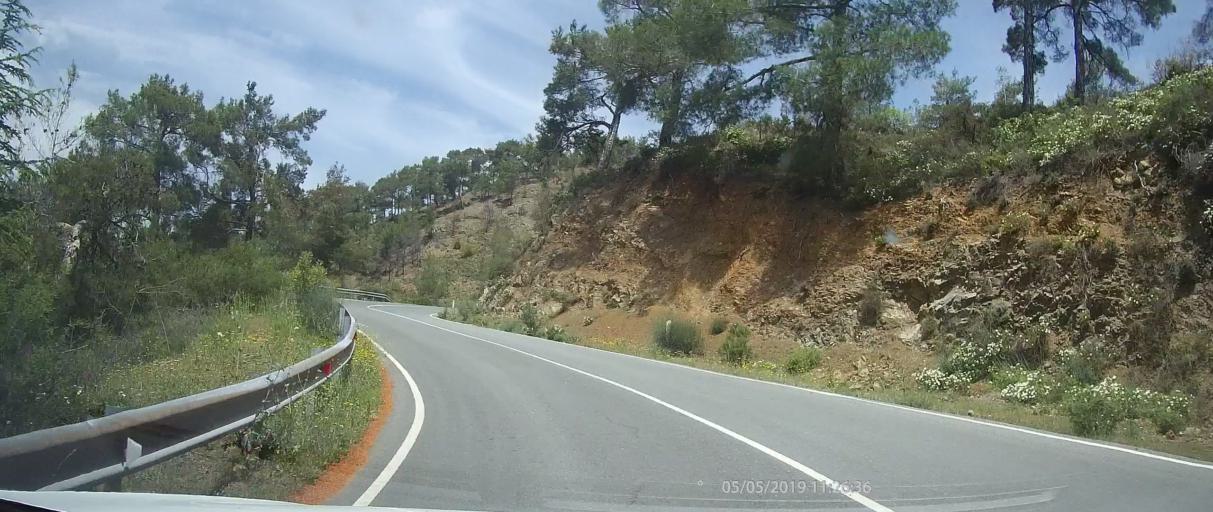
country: CY
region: Limassol
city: Pachna
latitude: 34.9297
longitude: 32.6468
